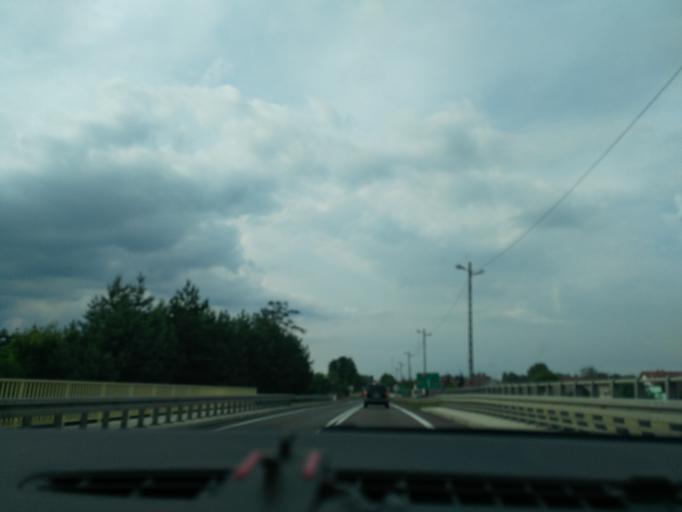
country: PL
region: Subcarpathian Voivodeship
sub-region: Powiat nizanski
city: Jezowe
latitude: 50.3731
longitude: 22.1272
